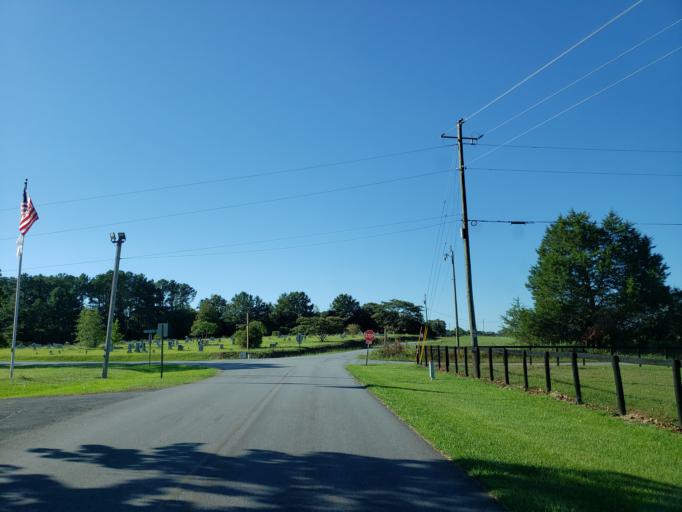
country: US
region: Georgia
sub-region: Bartow County
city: Euharlee
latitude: 34.1222
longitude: -85.0142
